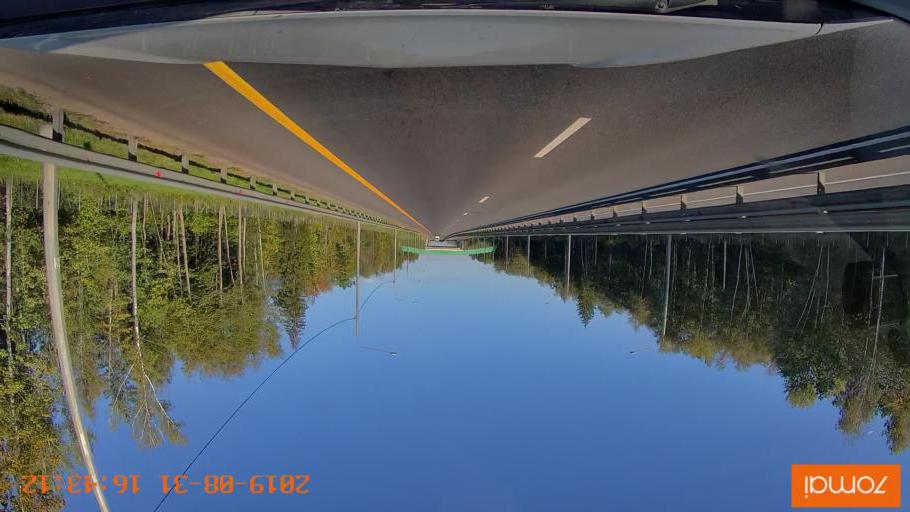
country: RU
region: Kaluga
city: Mstikhino
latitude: 54.6058
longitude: 36.1001
